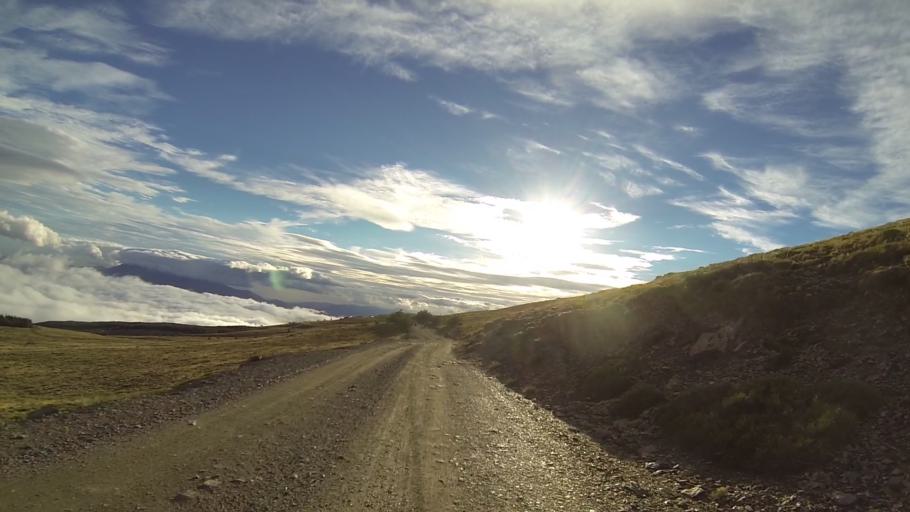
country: ES
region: Andalusia
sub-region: Provincia de Granada
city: Portugos
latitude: 36.9832
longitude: -3.3185
